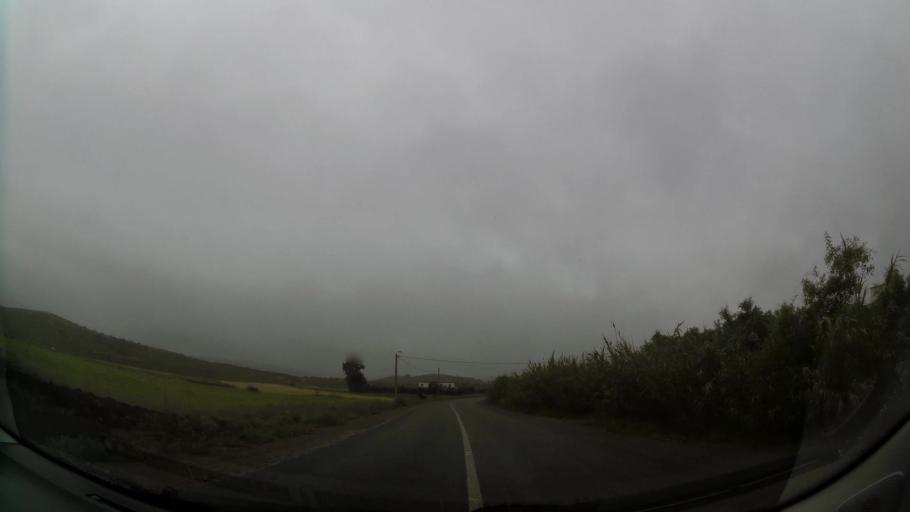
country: MA
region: Oriental
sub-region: Nador
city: Boudinar
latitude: 35.1113
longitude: -3.5738
